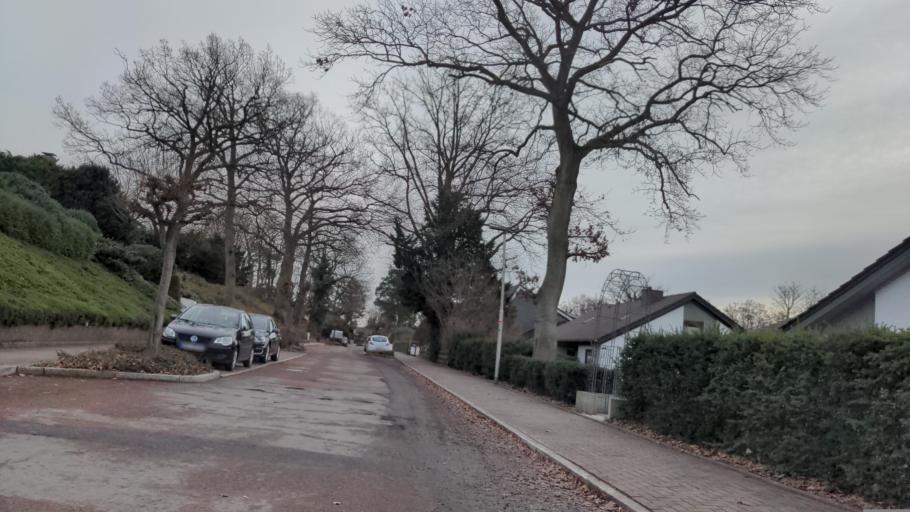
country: DE
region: Schleswig-Holstein
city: Malente
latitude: 54.1701
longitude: 10.5673
